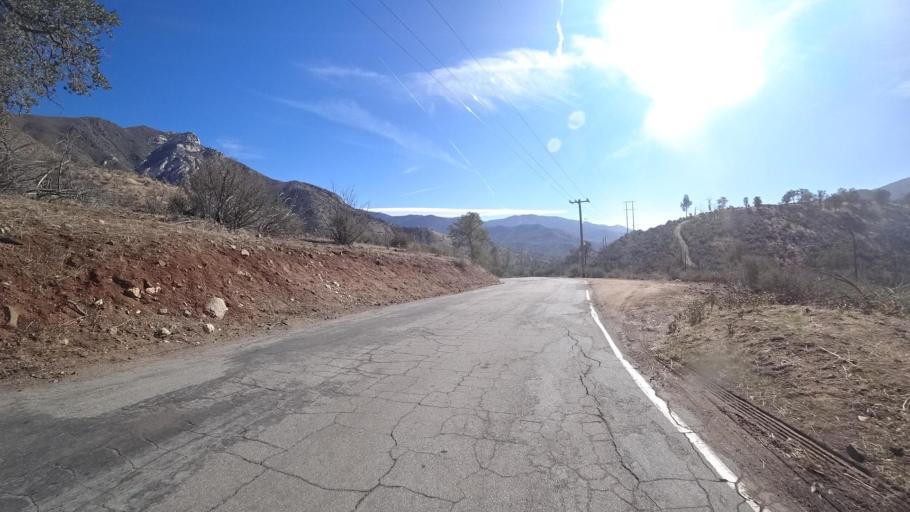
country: US
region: California
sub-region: Kern County
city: Bodfish
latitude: 35.5555
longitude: -118.5074
